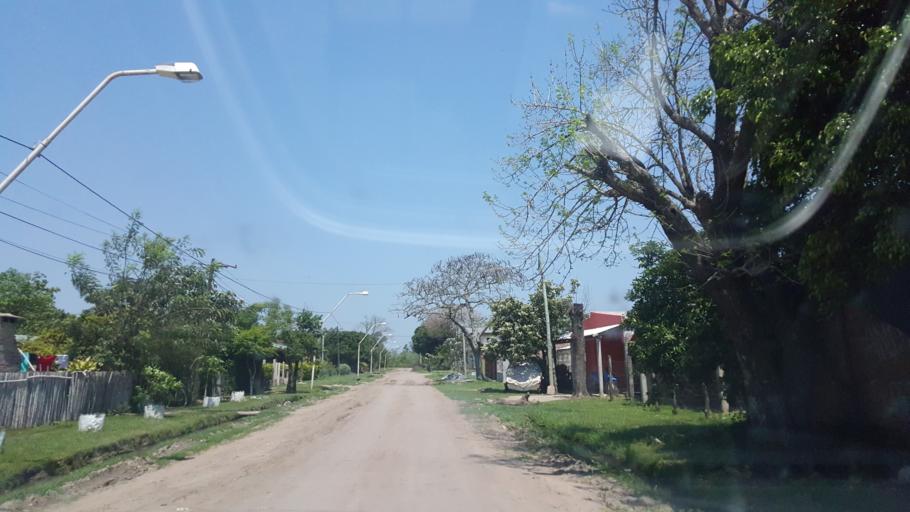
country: AR
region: Corrientes
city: Ita Ibate
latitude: -27.4257
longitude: -57.3292
